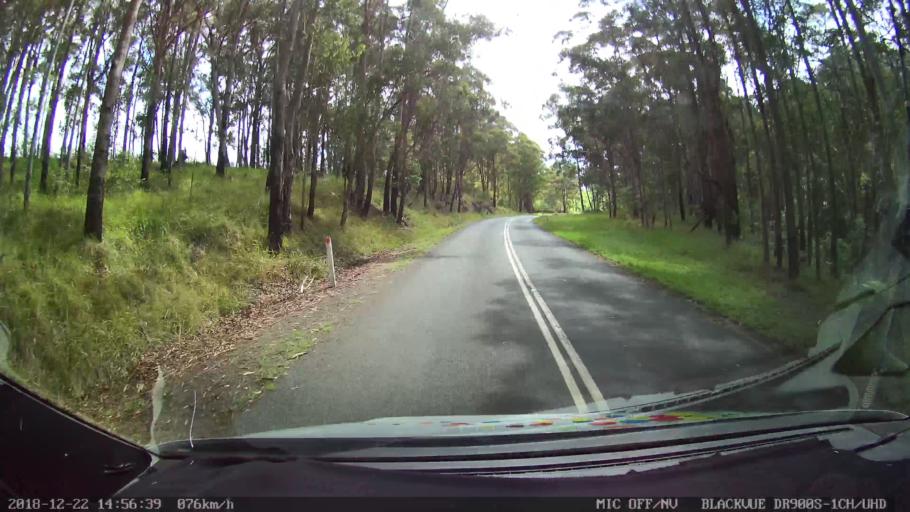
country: AU
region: New South Wales
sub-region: Bellingen
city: Dorrigo
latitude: -30.2341
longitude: 152.5101
